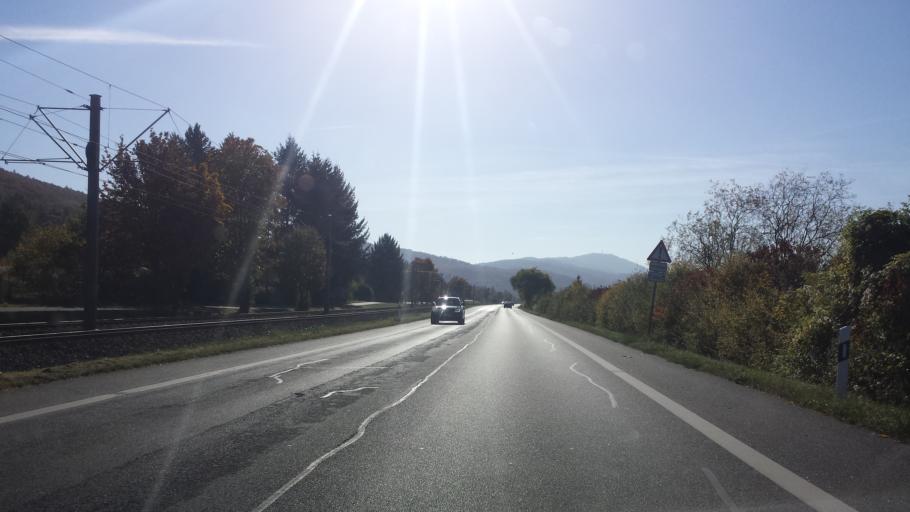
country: DE
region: Hesse
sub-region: Regierungsbezirk Darmstadt
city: Seeheim-Jugenheim
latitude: 49.7856
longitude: 8.6485
